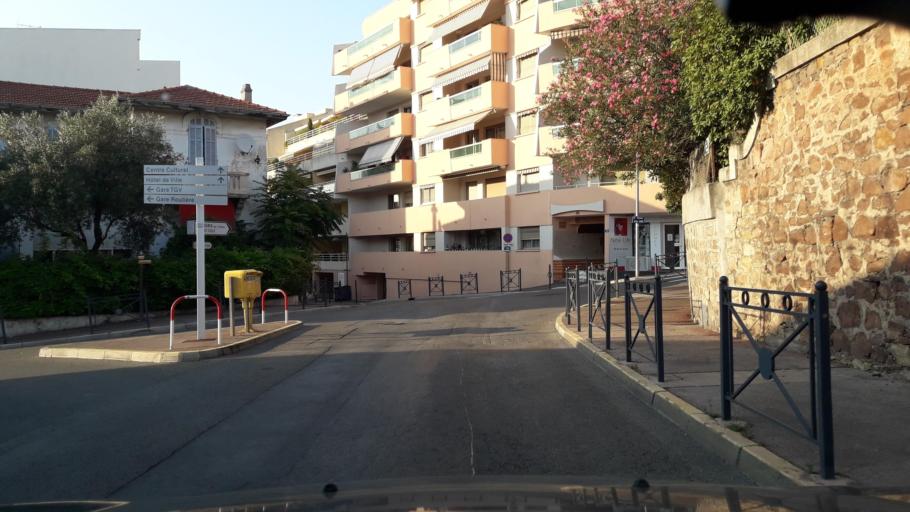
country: FR
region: Provence-Alpes-Cote d'Azur
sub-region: Departement du Var
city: Saint-Raphael
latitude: 43.4230
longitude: 6.7712
